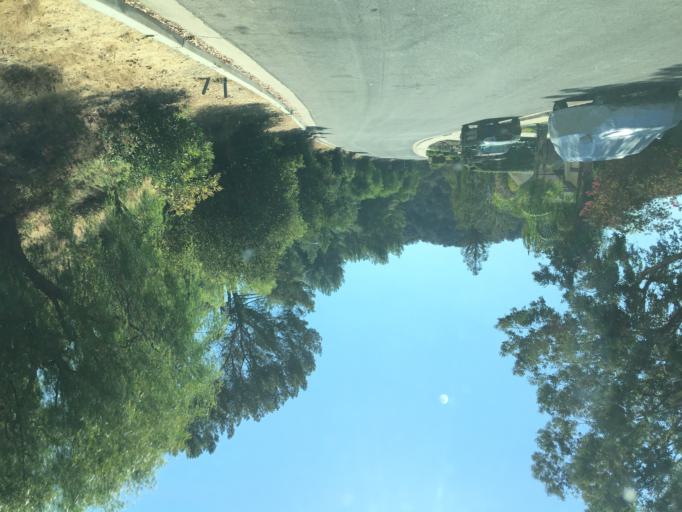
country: US
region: California
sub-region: Los Angeles County
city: Woodland Hills
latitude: 34.1418
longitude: -118.6005
